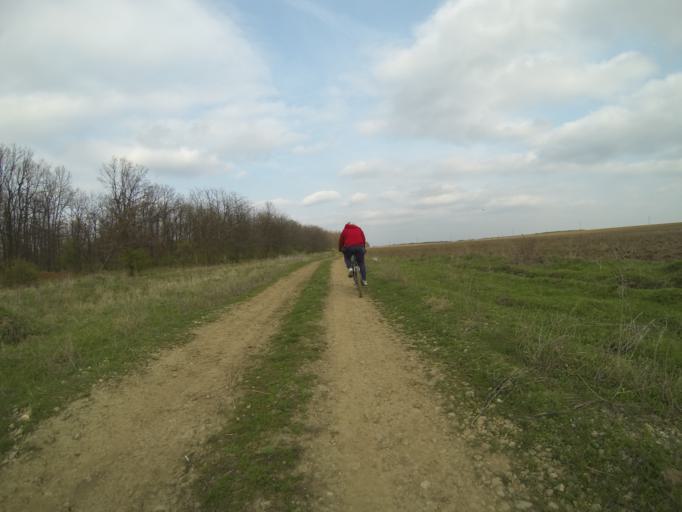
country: RO
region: Dolj
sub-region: Comuna Podari
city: Podari
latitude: 44.2475
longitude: 23.7405
